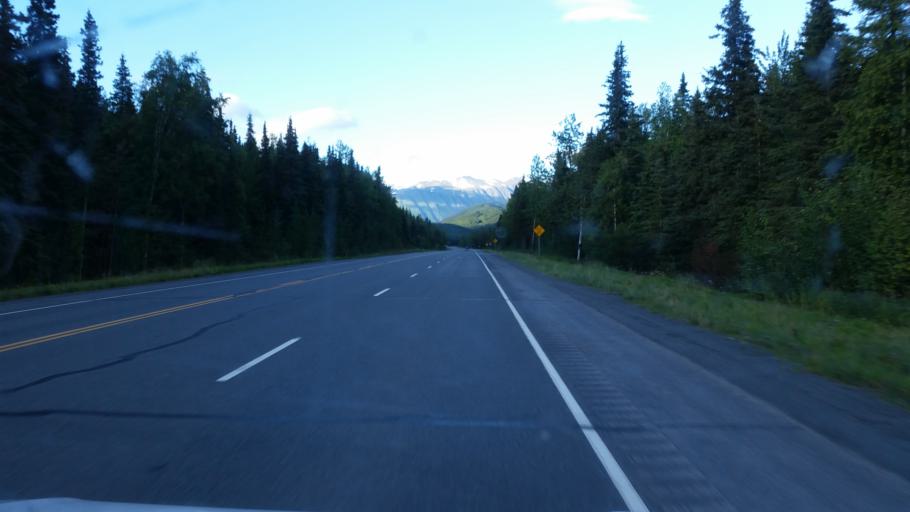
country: US
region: Alaska
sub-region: Kenai Peninsula Borough
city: Bear Creek
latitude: 60.4886
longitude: -149.7200
